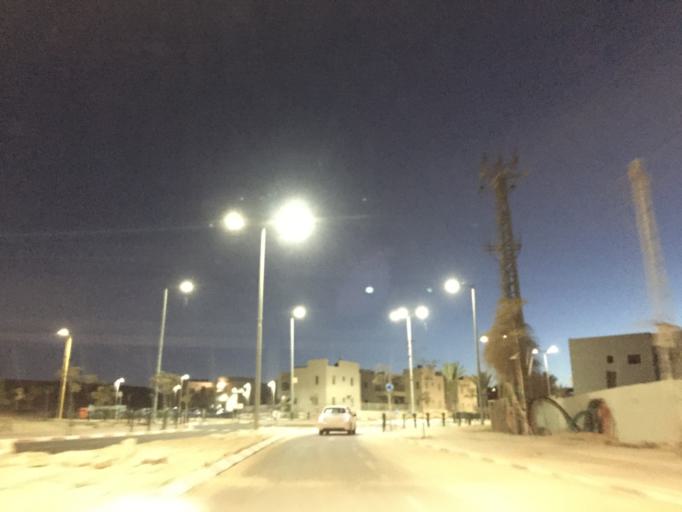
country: IL
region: Southern District
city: Mitzpe Ramon
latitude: 30.6172
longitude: 34.8006
